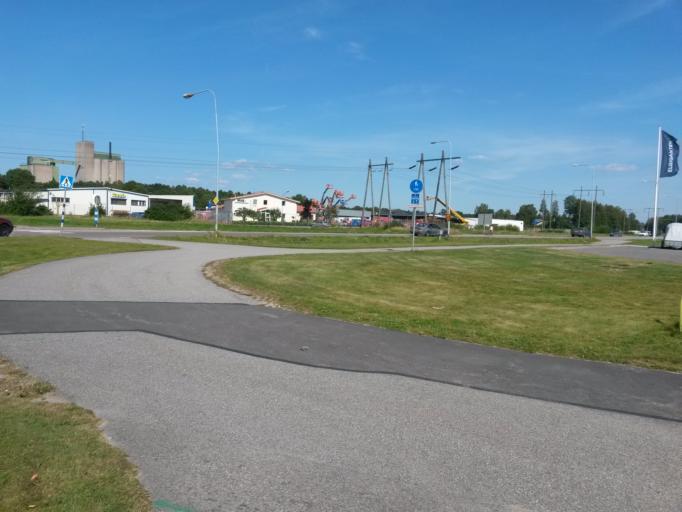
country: SE
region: Vaestra Goetaland
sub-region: Lidkopings Kommun
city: Lidkoping
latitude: 58.4964
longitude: 13.1814
